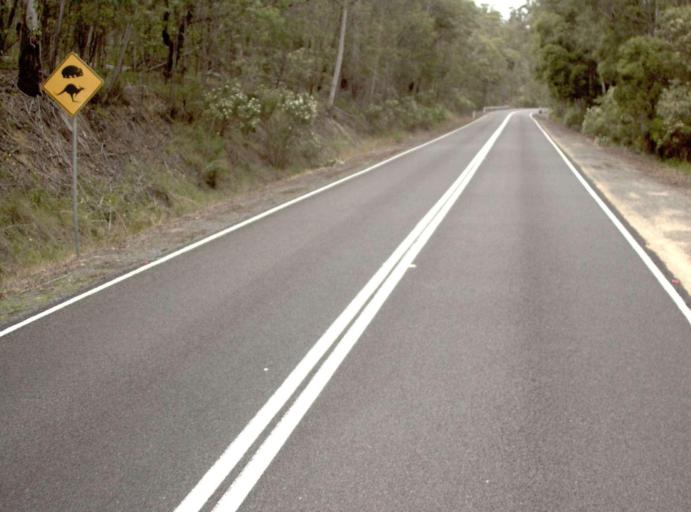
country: AU
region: New South Wales
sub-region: Bombala
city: Bombala
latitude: -37.2694
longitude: 149.2273
